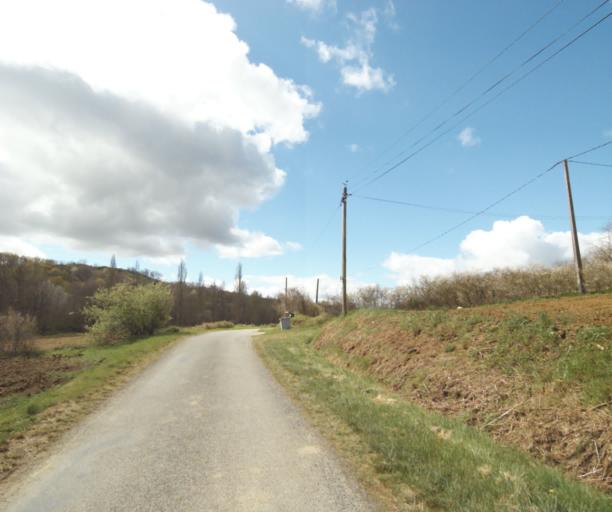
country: FR
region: Midi-Pyrenees
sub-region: Departement de l'Ariege
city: Saverdun
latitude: 43.1946
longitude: 1.5666
